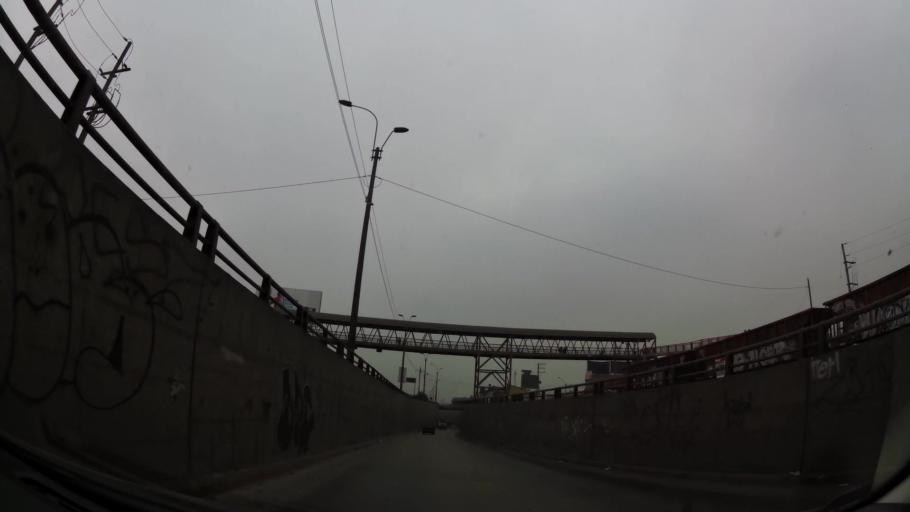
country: PE
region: Lima
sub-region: Lima
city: Santa Maria
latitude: -12.0176
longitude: -76.8943
